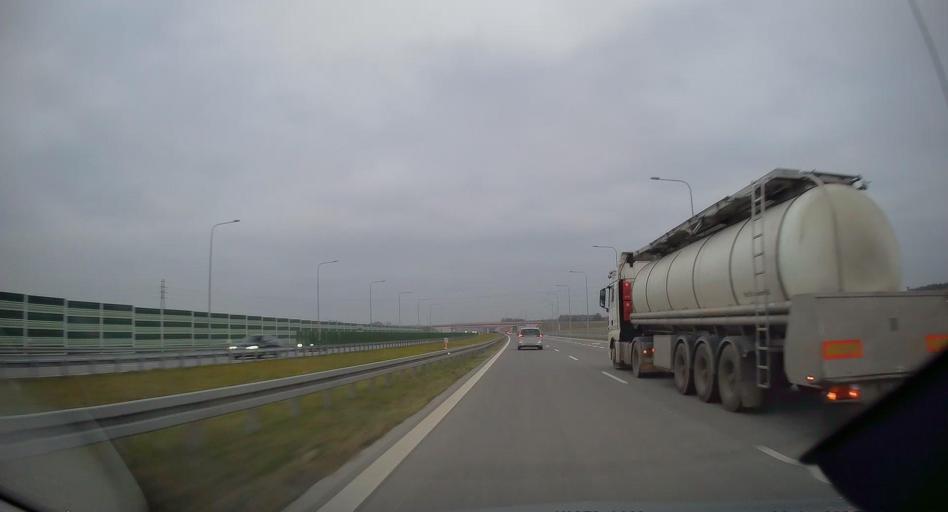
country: PL
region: Silesian Voivodeship
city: Wozniki
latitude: 50.6019
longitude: 19.0327
